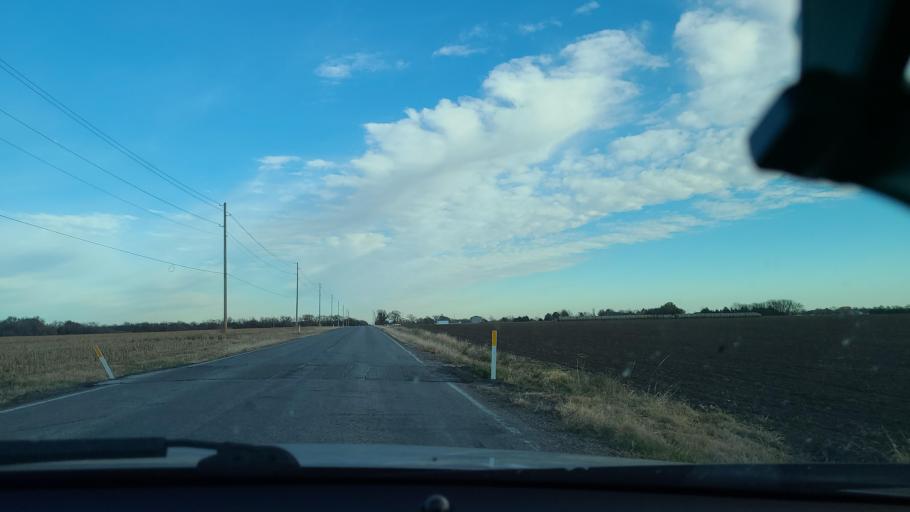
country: US
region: Kansas
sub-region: Sedgwick County
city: Goddard
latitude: 37.6498
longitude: -97.5423
